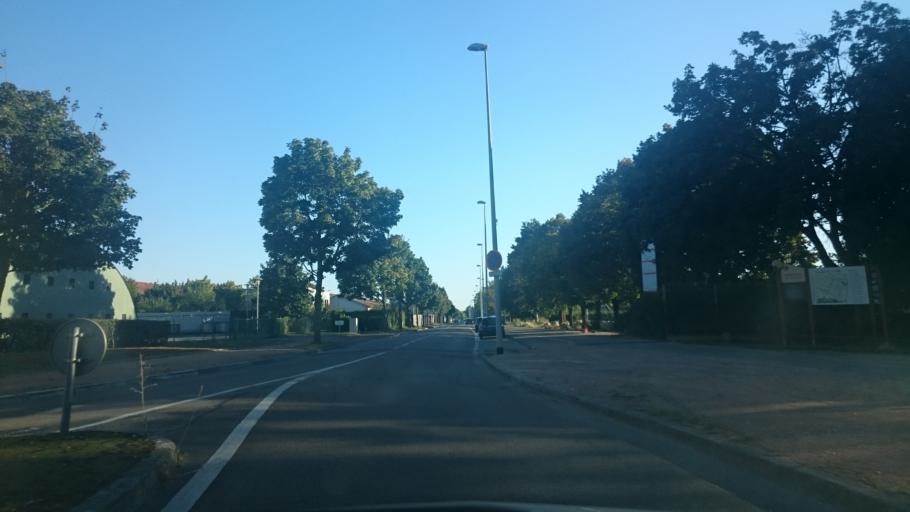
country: FR
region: Bourgogne
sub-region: Departement de la Cote-d'Or
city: Saint-Apollinaire
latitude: 47.3444
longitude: 5.0587
